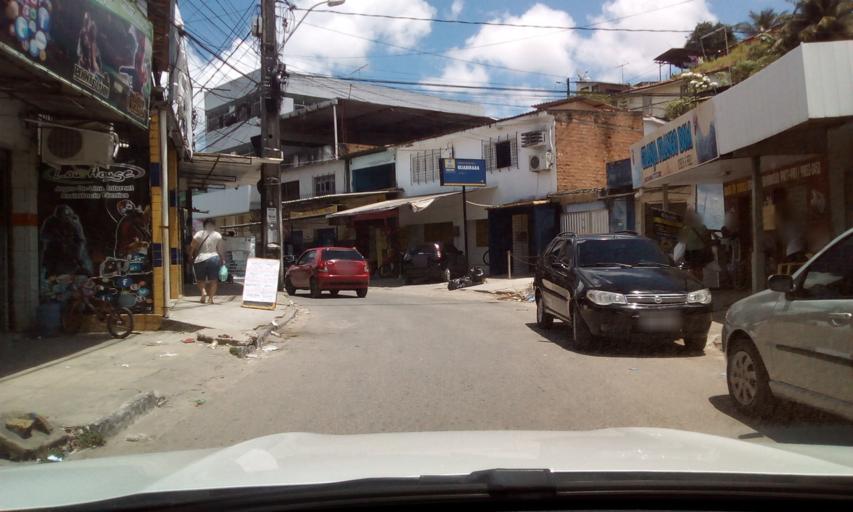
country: BR
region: Pernambuco
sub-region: Recife
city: Recife
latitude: -7.9938
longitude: -34.9364
